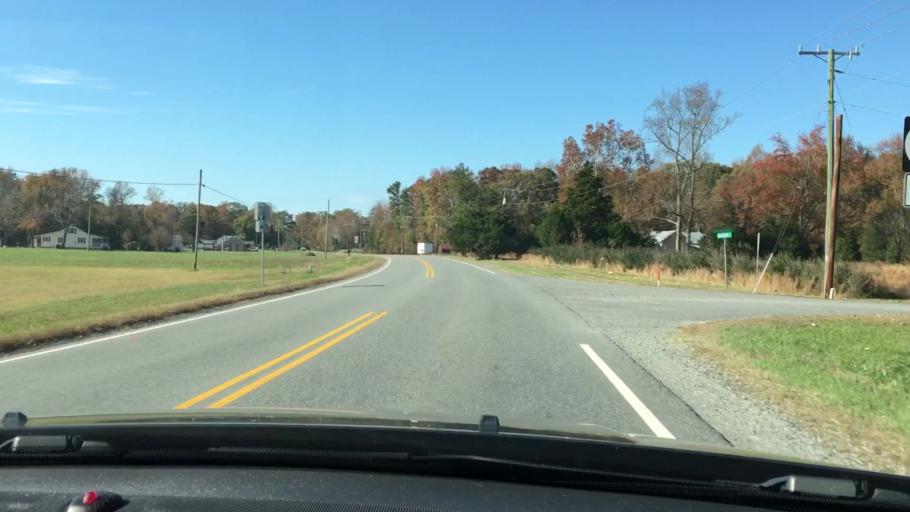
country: US
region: Virginia
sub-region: King William County
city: King William
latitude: 37.6722
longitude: -76.9741
